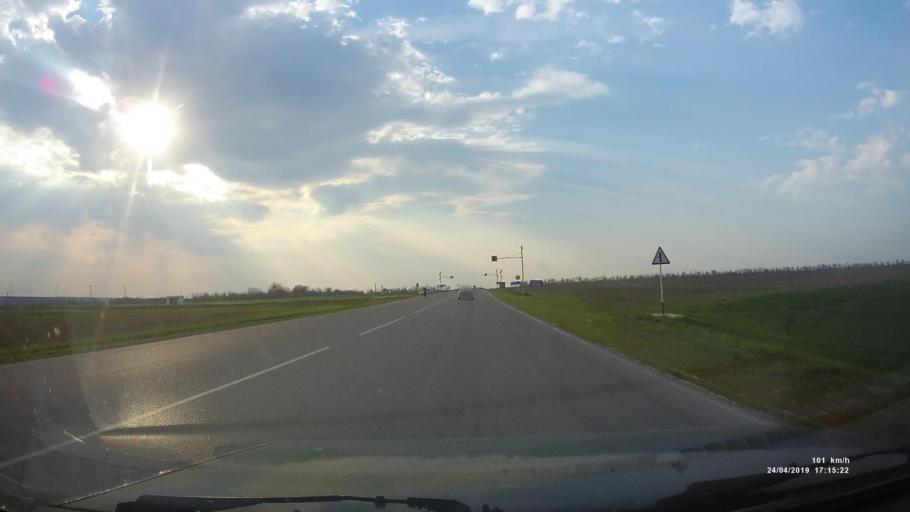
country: RU
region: Rostov
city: Sal'sk
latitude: 46.4886
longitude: 41.4440
